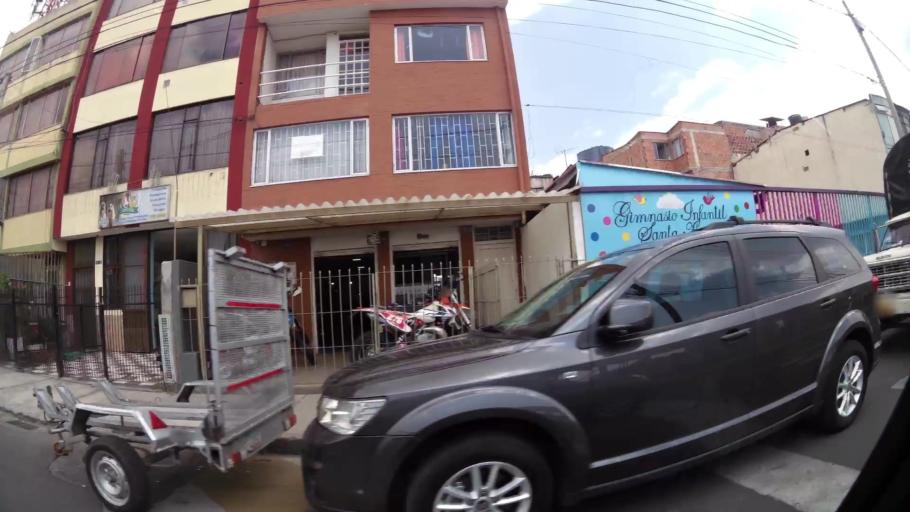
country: CO
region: Cundinamarca
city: La Calera
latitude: 4.7349
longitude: -74.0277
